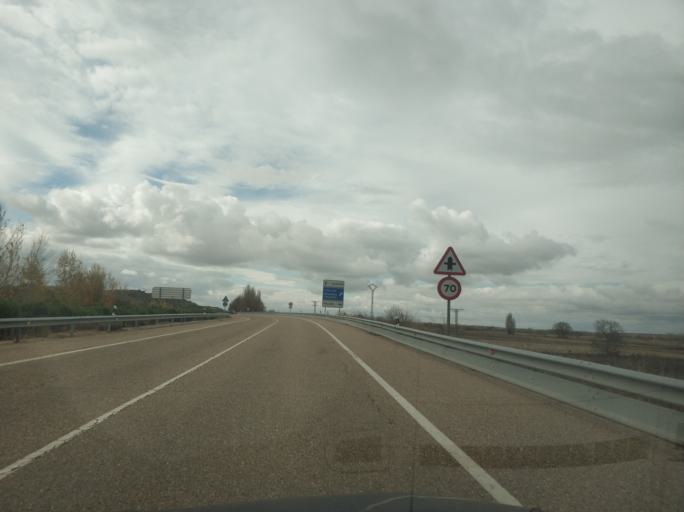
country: ES
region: Castille and Leon
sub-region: Provincia de Valladolid
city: Torrecilla de la Abadesa
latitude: 41.4548
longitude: -5.0861
